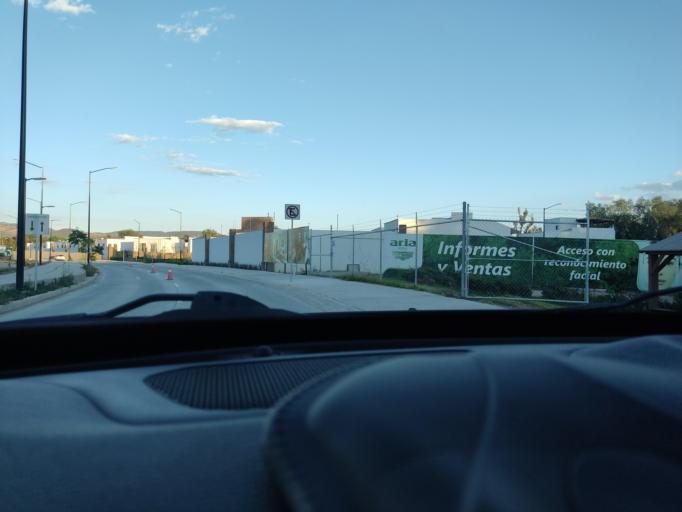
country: MX
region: Guanajuato
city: Leon
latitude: 21.1560
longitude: -101.6638
